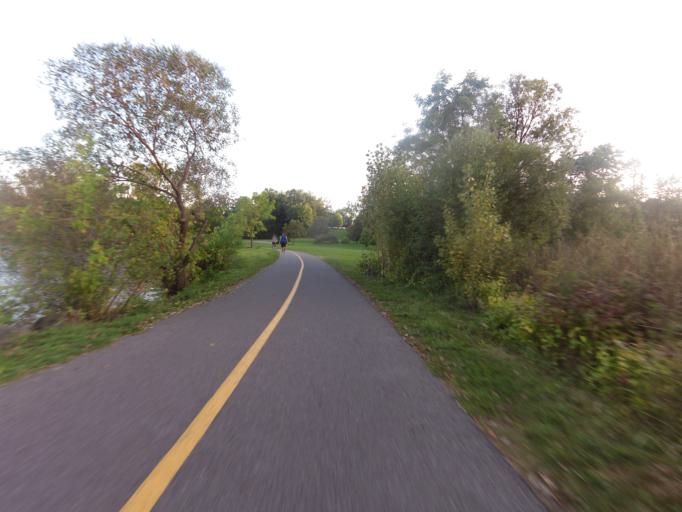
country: CA
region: Ontario
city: Ottawa
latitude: 45.3935
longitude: -75.7040
